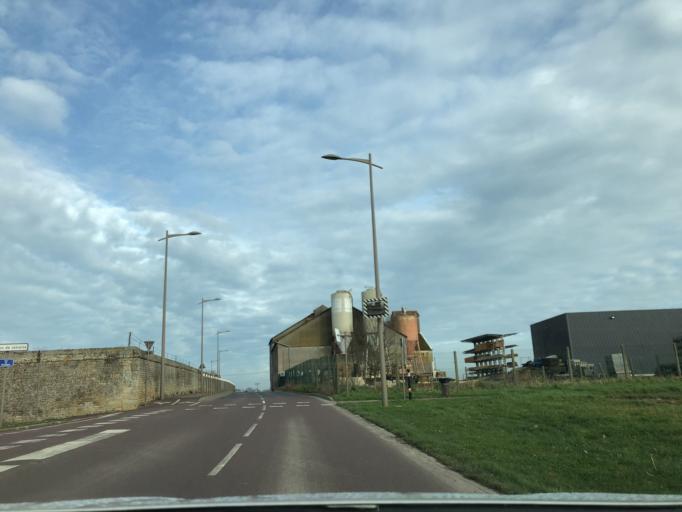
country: FR
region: Lower Normandy
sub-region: Departement du Calvados
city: Douvres-la-Delivrande
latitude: 49.2935
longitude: -0.3673
